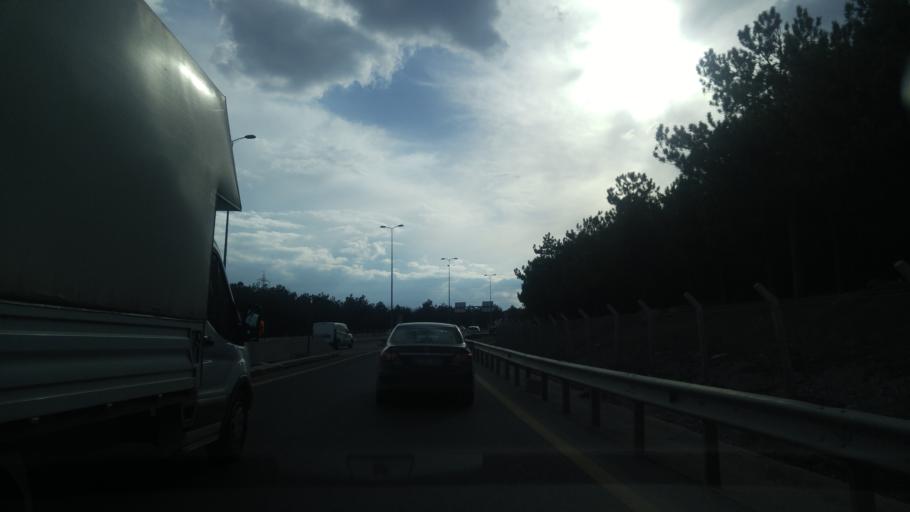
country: TR
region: Ankara
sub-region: Goelbasi
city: Golbasi
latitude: 39.8435
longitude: 32.8042
